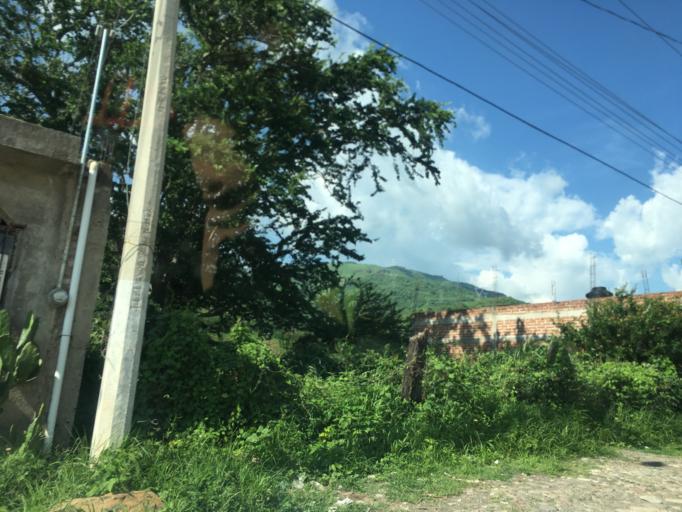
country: MX
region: Nayarit
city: Ixtlan del Rio
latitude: 21.0450
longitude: -104.3615
